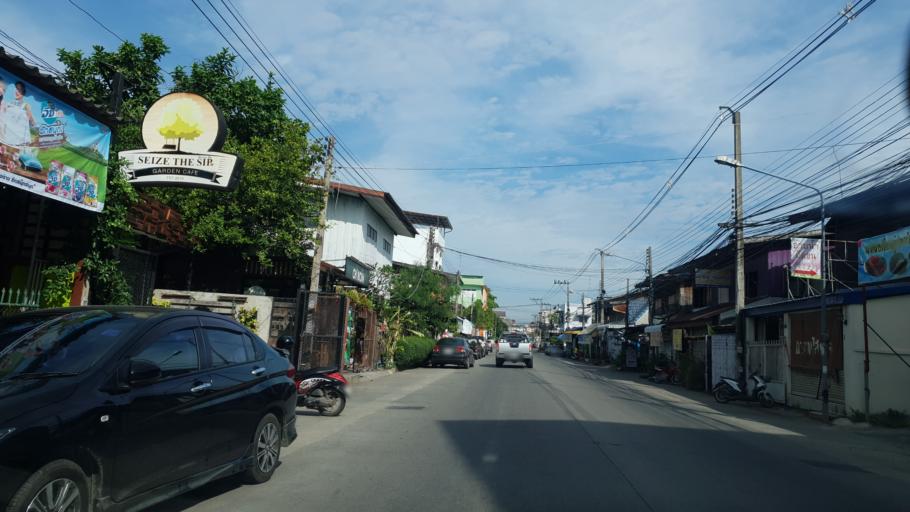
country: TH
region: Phitsanulok
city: Phitsanulok
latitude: 16.8094
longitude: 100.2676
